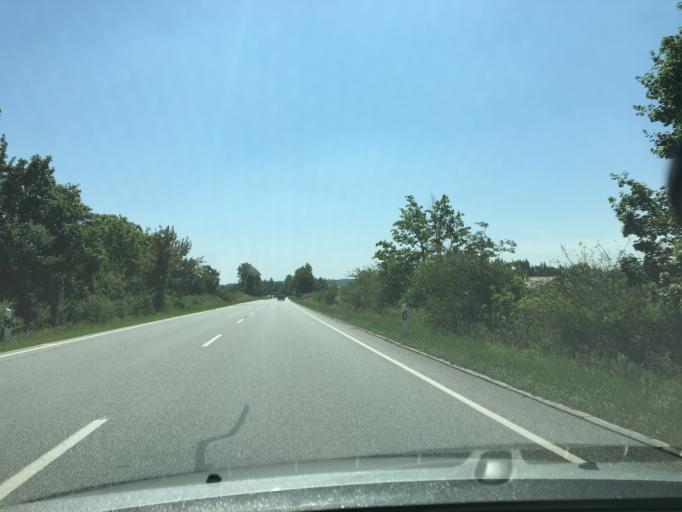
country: DE
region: Bavaria
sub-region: Lower Bavaria
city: Geisenhausen
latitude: 48.4911
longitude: 12.2328
